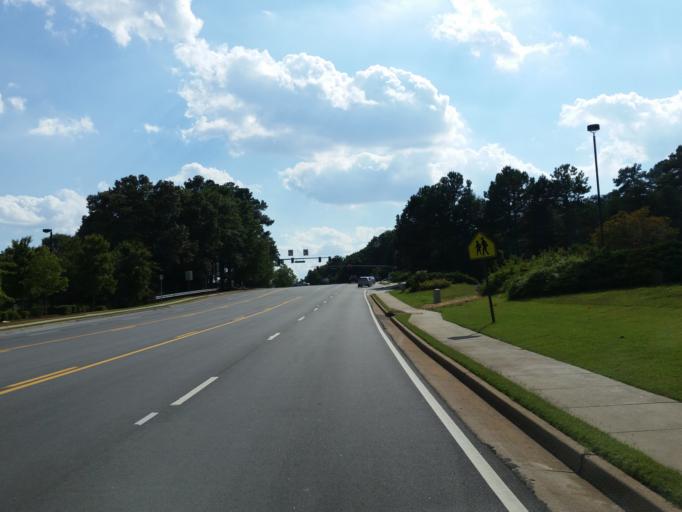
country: US
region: Georgia
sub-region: Gwinnett County
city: Duluth
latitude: 33.9469
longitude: -84.1341
